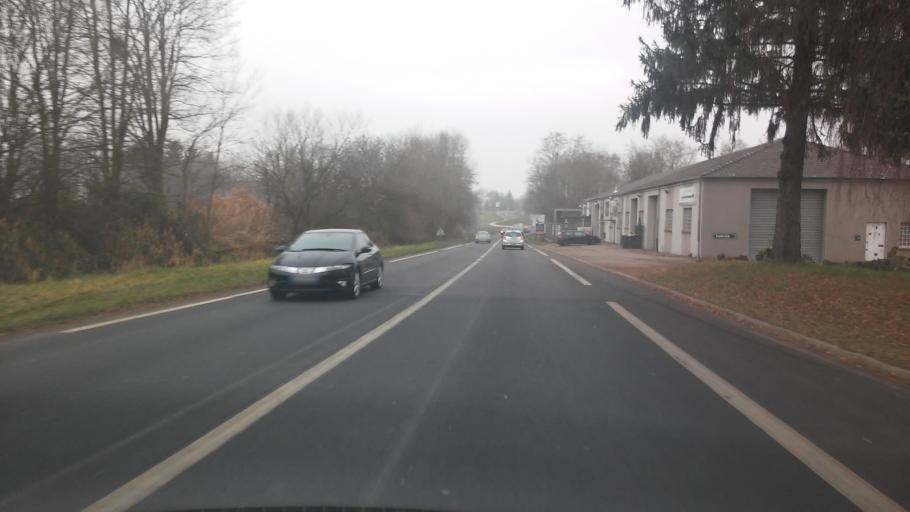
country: FR
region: Lorraine
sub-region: Departement de la Moselle
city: Marly
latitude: 49.0619
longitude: 6.1359
